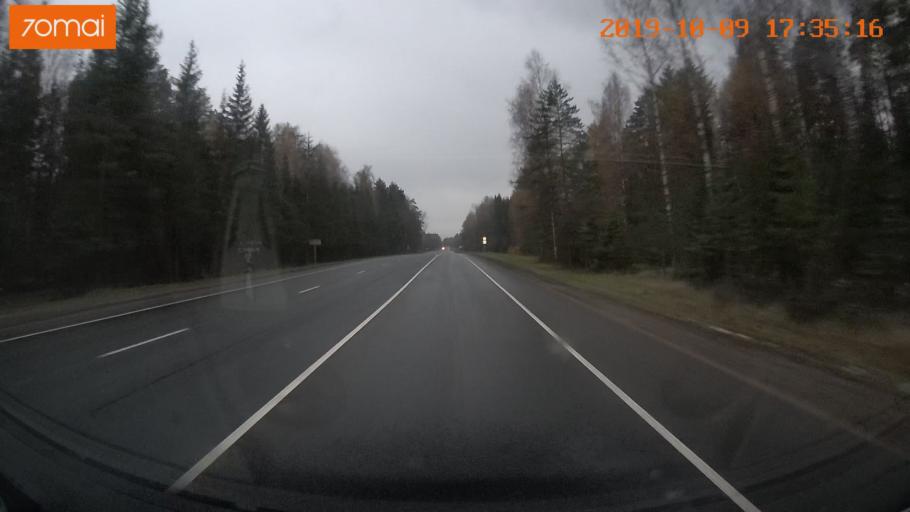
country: RU
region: Ivanovo
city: Bogorodskoye
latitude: 57.0962
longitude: 41.0033
